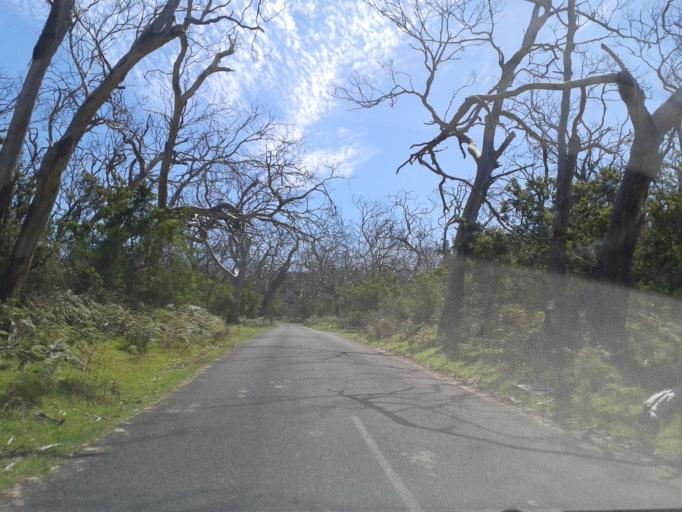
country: AU
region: Victoria
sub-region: Colac-Otway
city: Apollo Bay
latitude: -38.8422
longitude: 143.5345
